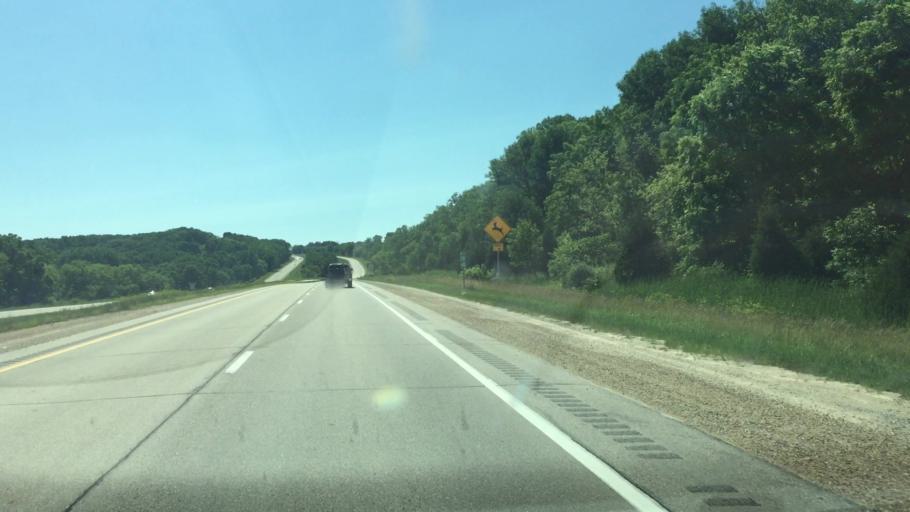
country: US
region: Iowa
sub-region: Dubuque County
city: Dubuque
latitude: 42.4188
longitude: -90.7038
